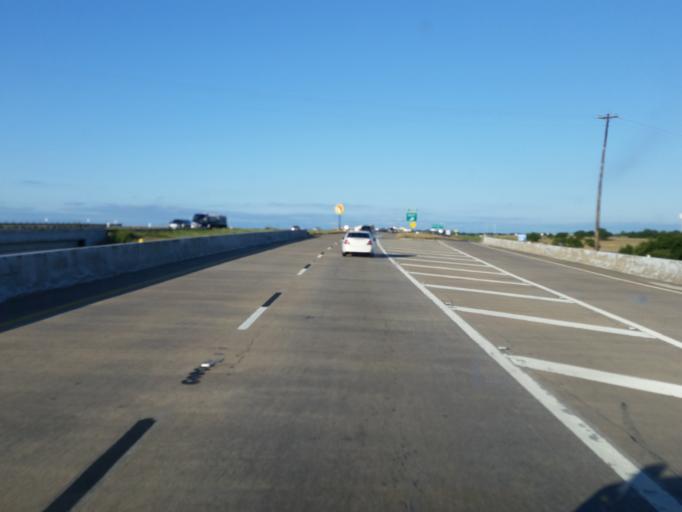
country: US
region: Texas
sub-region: Kaufman County
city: Terrell
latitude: 32.7148
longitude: -96.3305
